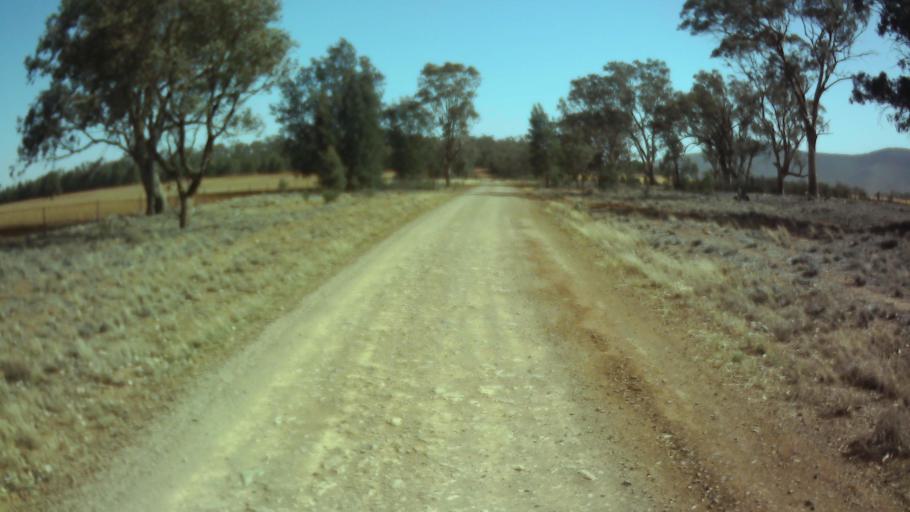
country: AU
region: New South Wales
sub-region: Weddin
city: Grenfell
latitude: -33.8572
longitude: 148.0156
